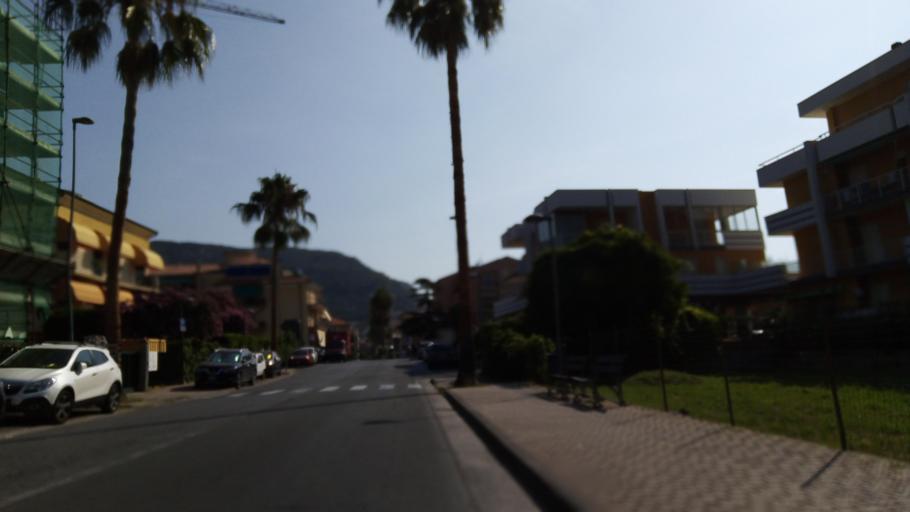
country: IT
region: Liguria
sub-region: Provincia di Savona
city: Borgio
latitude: 44.1571
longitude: 8.3015
